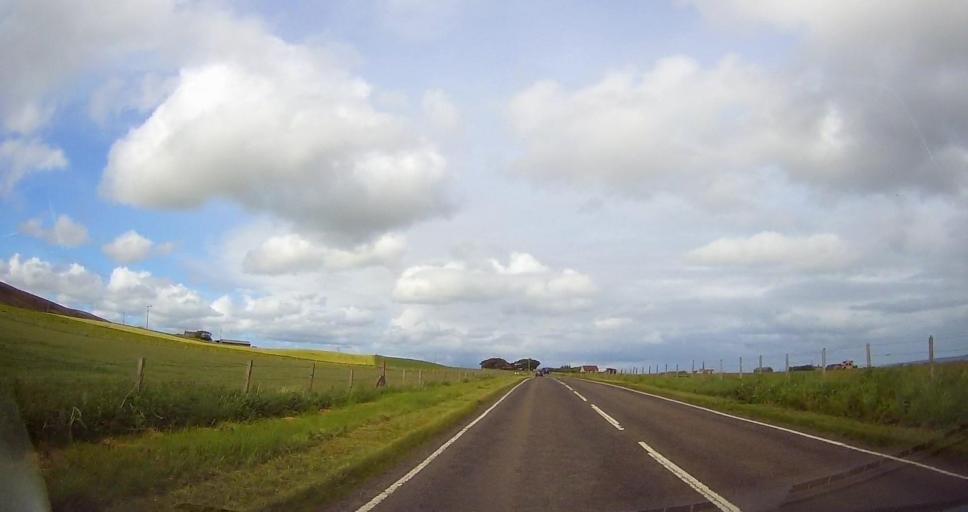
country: GB
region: Scotland
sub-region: Orkney Islands
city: Orkney
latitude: 59.0189
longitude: -3.1022
